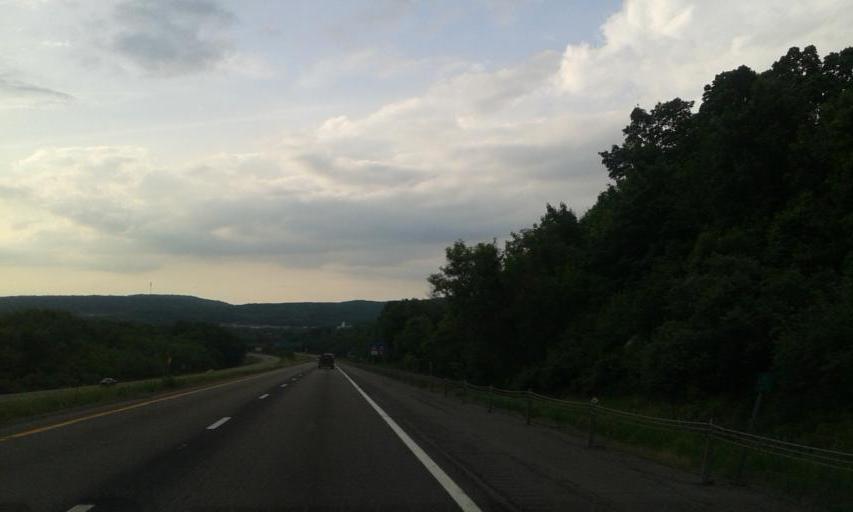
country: US
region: New York
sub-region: Broome County
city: Chenango Bridge
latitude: 42.0881
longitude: -75.8100
